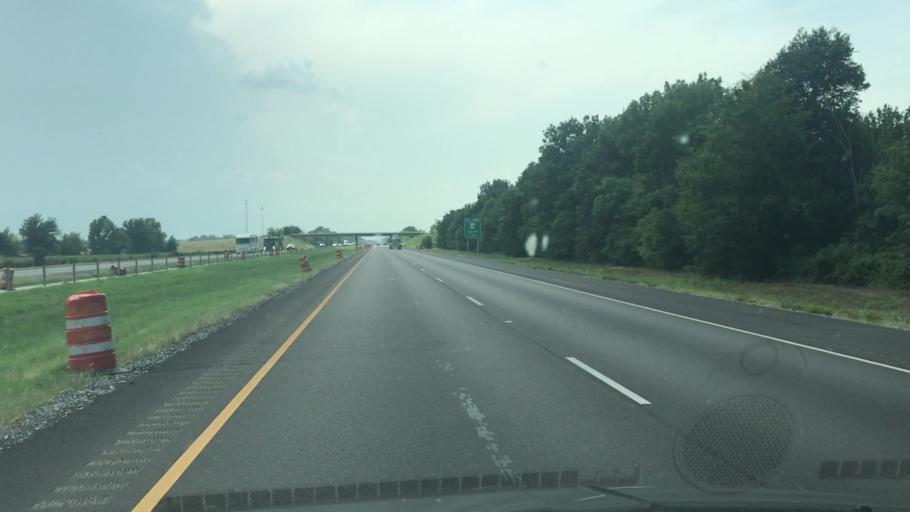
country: US
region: Arkansas
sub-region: Crittenden County
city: Earle
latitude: 35.1336
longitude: -90.4620
